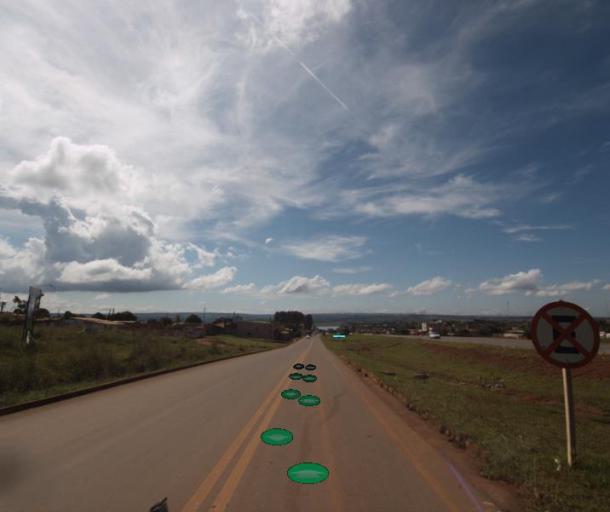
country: BR
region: Federal District
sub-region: Brasilia
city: Brasilia
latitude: -15.7590
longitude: -48.2485
